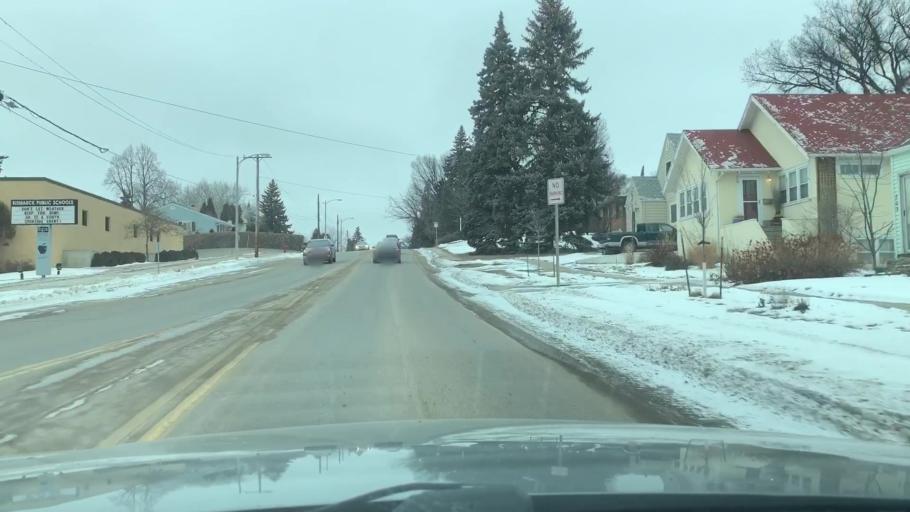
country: US
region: North Dakota
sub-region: Burleigh County
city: Bismarck
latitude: 46.8132
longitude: -100.7943
